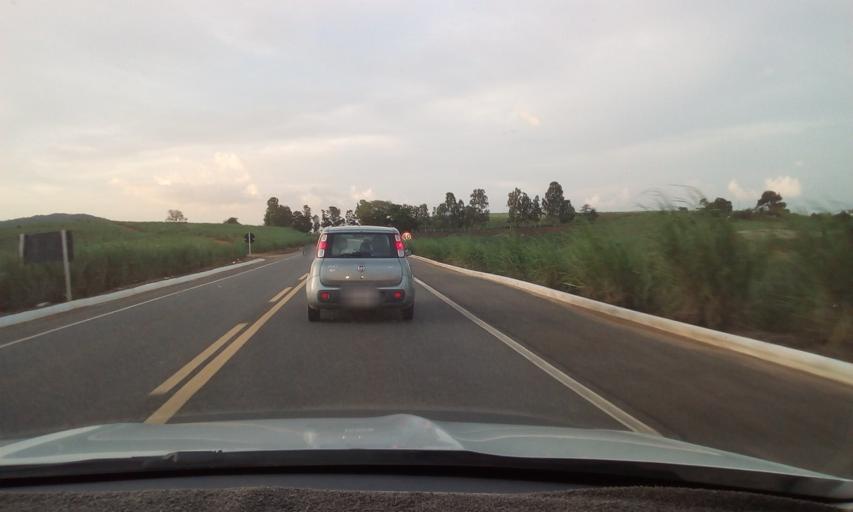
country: BR
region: Pernambuco
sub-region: Vicencia
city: Vicencia
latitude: -7.6042
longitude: -35.2408
